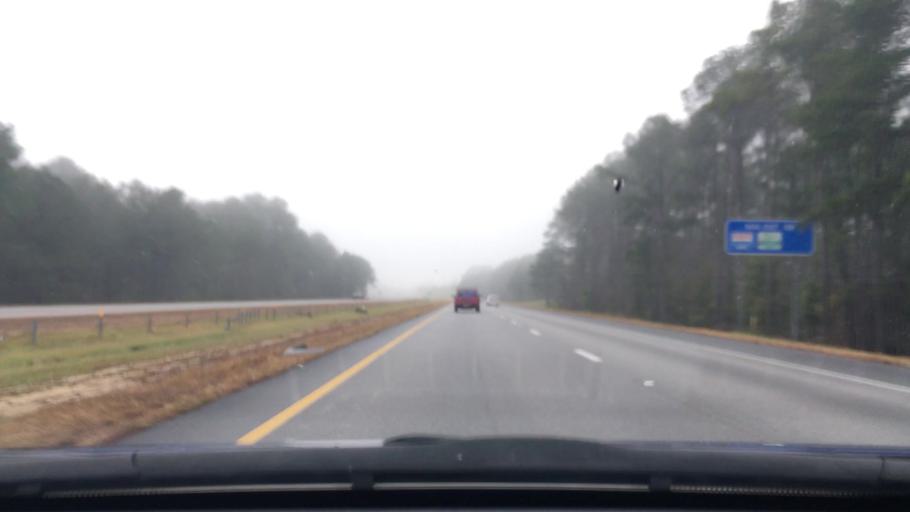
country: US
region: South Carolina
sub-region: Lee County
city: Bishopville
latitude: 34.2117
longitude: -80.4085
